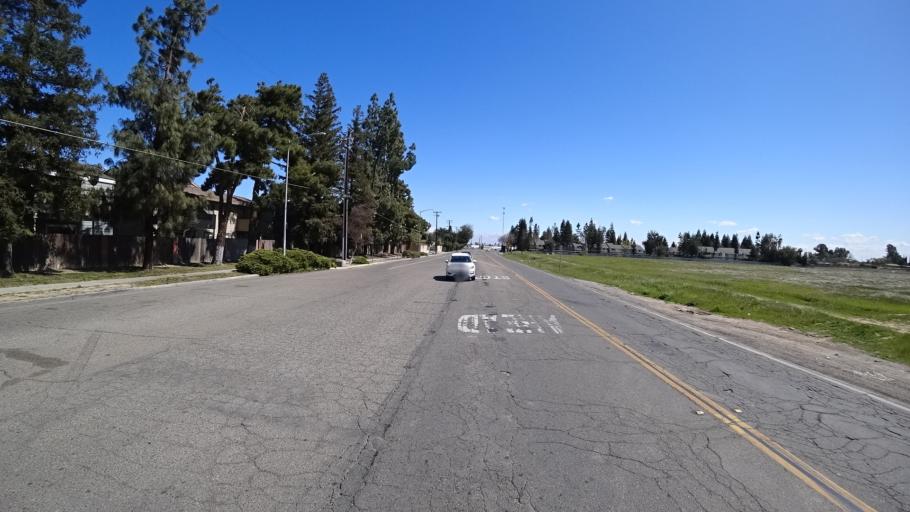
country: US
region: California
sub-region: Fresno County
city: West Park
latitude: 36.7792
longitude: -119.8521
